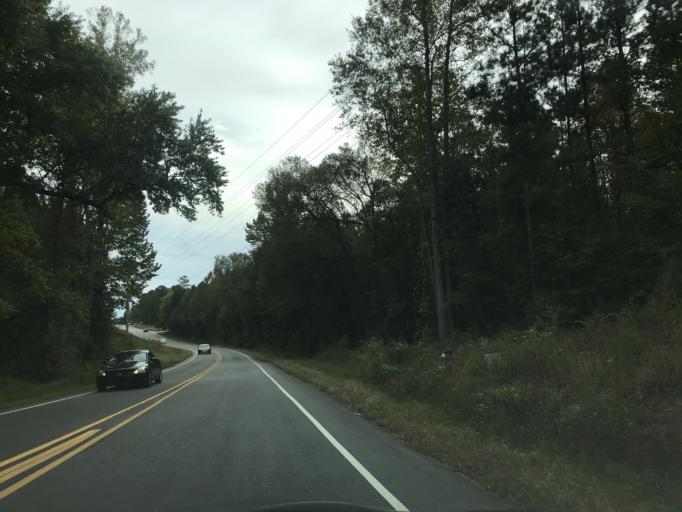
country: US
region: North Carolina
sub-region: Wake County
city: Rolesville
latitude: 35.9015
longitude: -78.5068
